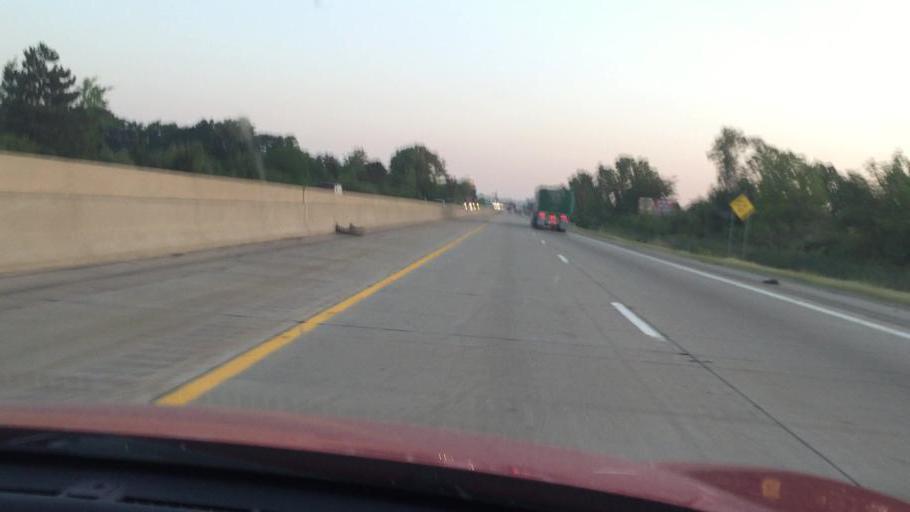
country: US
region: Michigan
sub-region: Monroe County
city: Dundee
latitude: 41.9437
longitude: -83.6645
